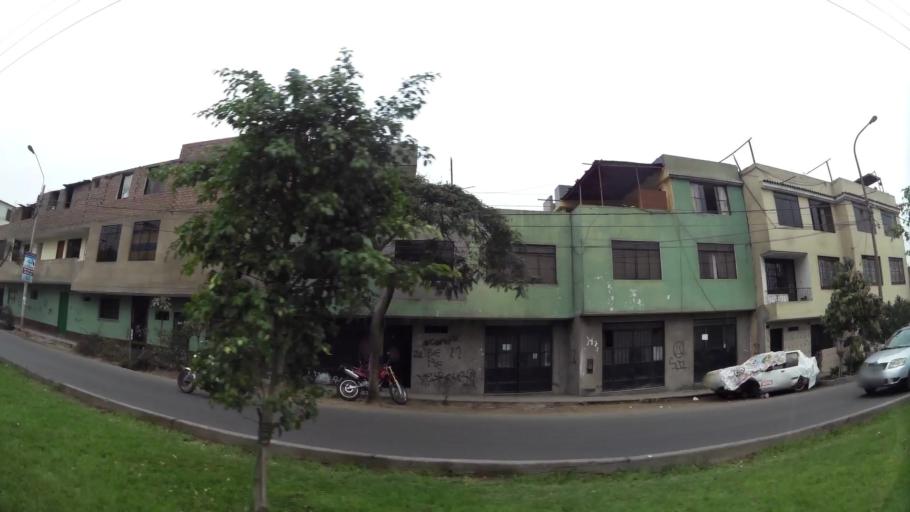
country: PE
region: Lima
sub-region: Lima
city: Independencia
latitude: -11.9635
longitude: -76.9941
